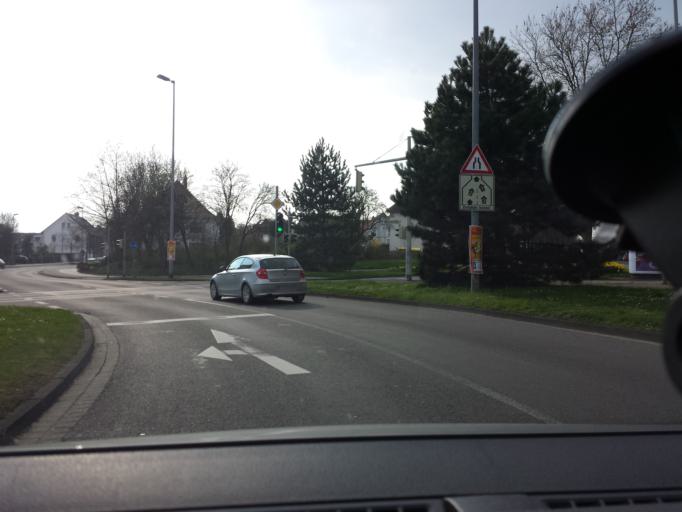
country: DE
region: Lower Saxony
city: Braunschweig
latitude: 52.2725
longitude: 10.4912
